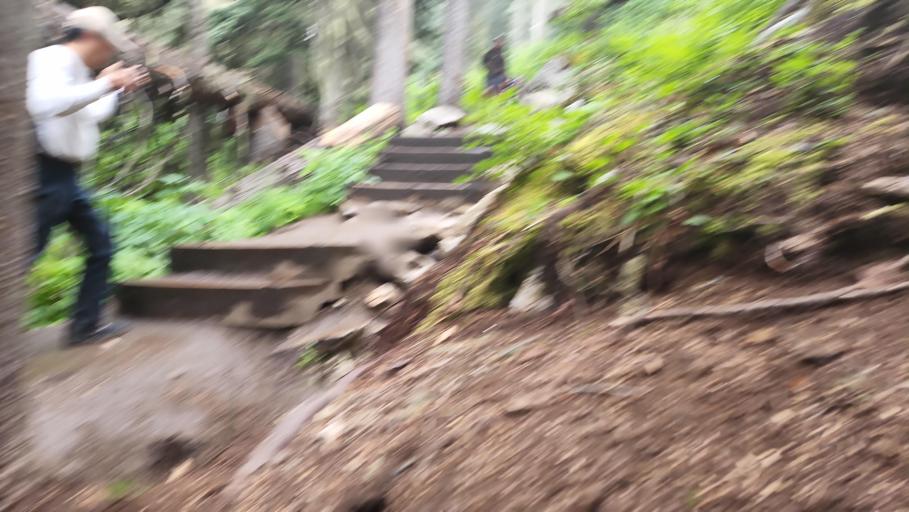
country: CA
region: British Columbia
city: Pemberton
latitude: 50.3576
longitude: -122.4879
